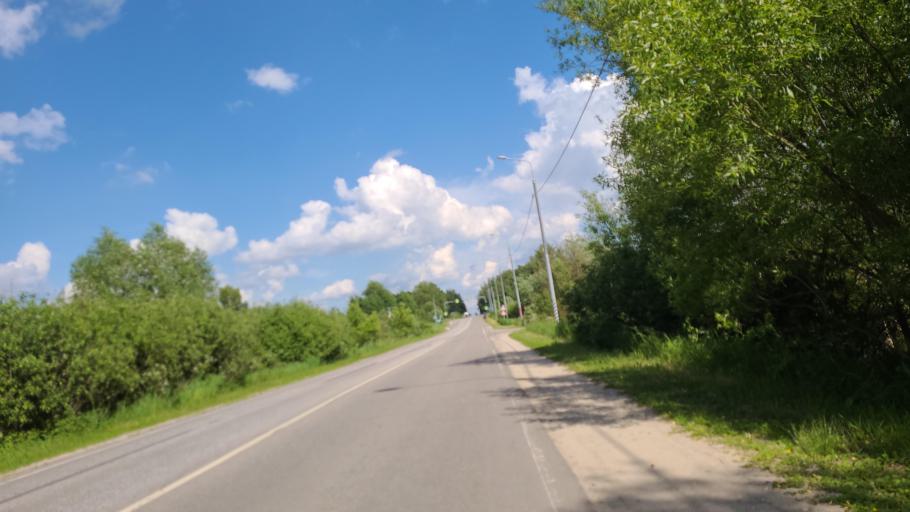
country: RU
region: Moskovskaya
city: Konobeyevo
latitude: 55.4018
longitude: 38.6708
